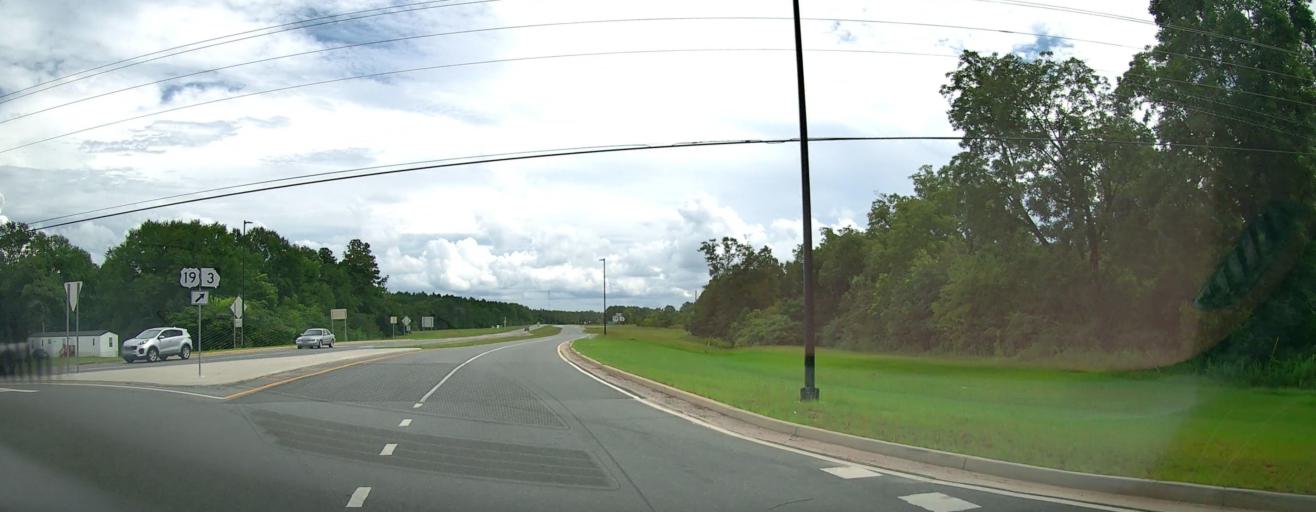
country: US
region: Georgia
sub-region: Schley County
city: Ellaville
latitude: 32.2398
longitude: -84.2963
